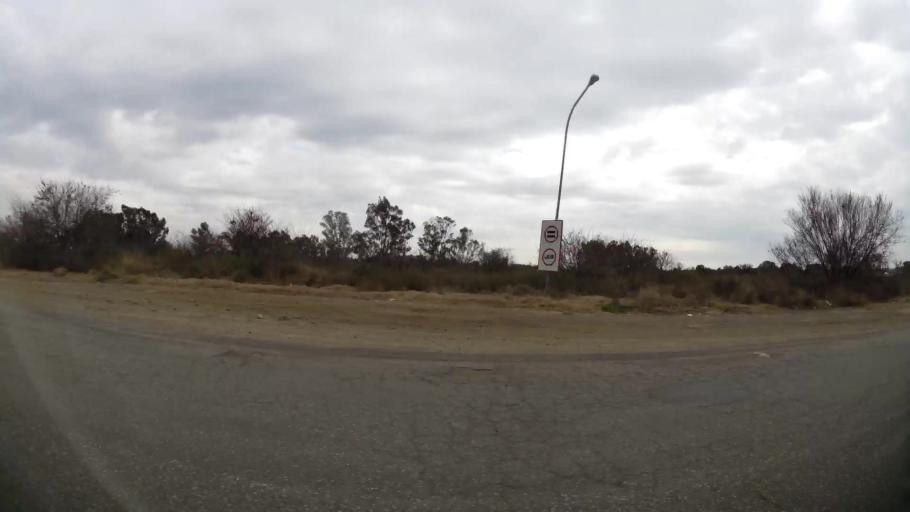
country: ZA
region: Orange Free State
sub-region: Fezile Dabi District Municipality
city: Kroonstad
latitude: -27.6715
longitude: 27.2302
